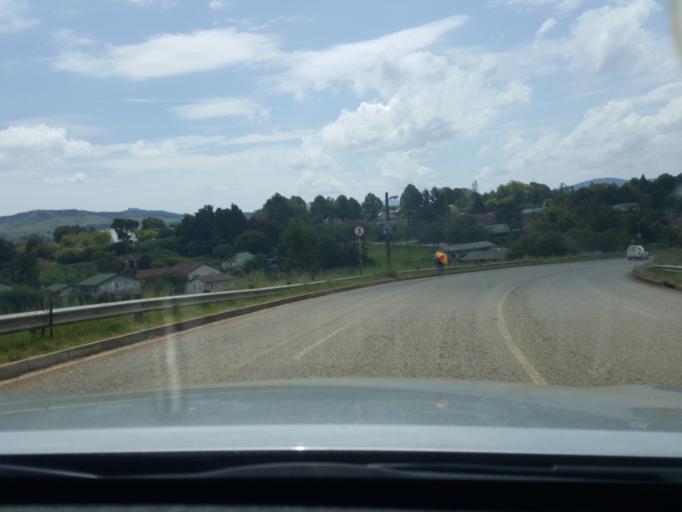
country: ZA
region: Mpumalanga
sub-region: Ehlanzeni District
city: Graksop
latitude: -24.9334
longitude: 30.8384
